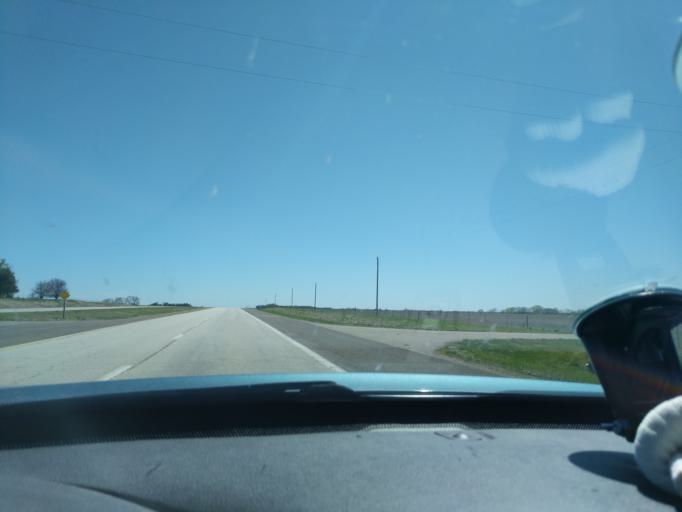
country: US
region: Kansas
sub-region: Republic County
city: Belleville
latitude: 39.7622
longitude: -97.6518
